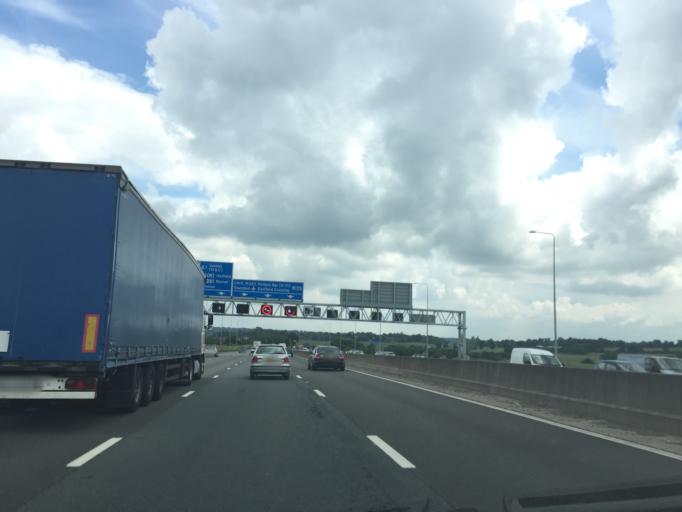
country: GB
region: England
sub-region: Hertfordshire
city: Shenley AV
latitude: 51.7048
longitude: -0.2509
